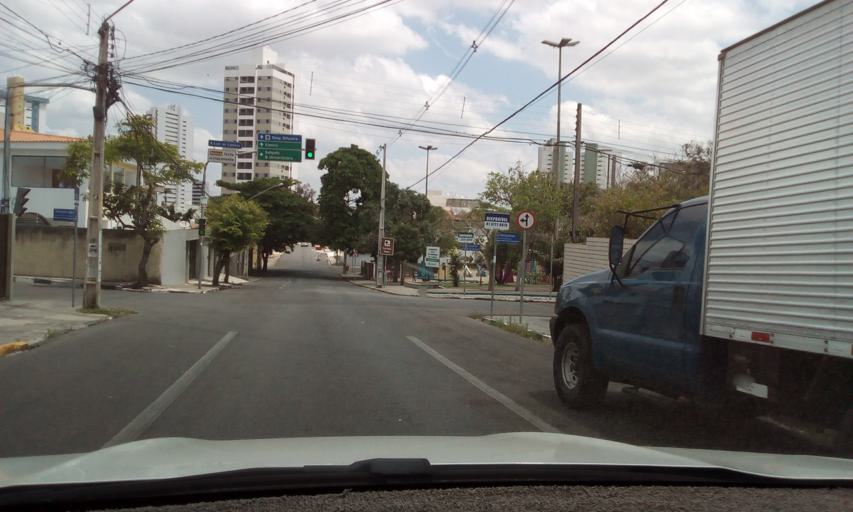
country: BR
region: Pernambuco
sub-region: Caruaru
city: Caruaru
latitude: -8.2757
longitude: -35.9705
